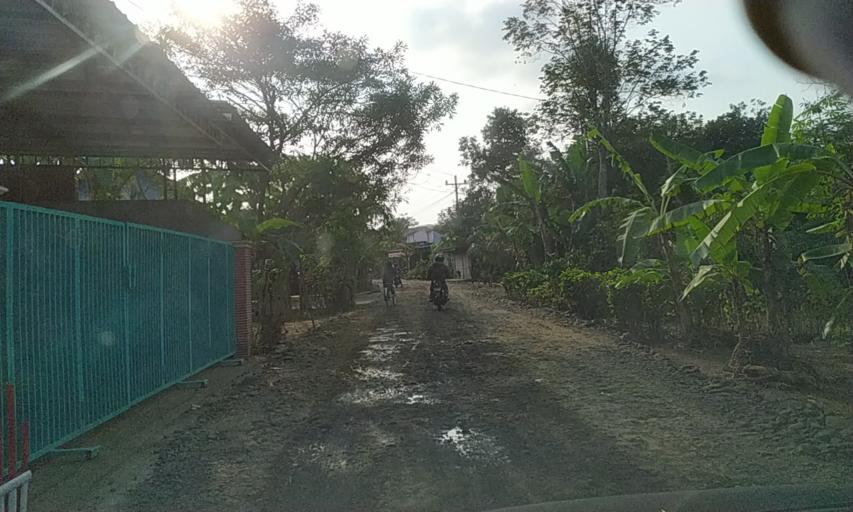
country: ID
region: Central Java
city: Mandala
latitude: -7.6052
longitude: 109.0668
